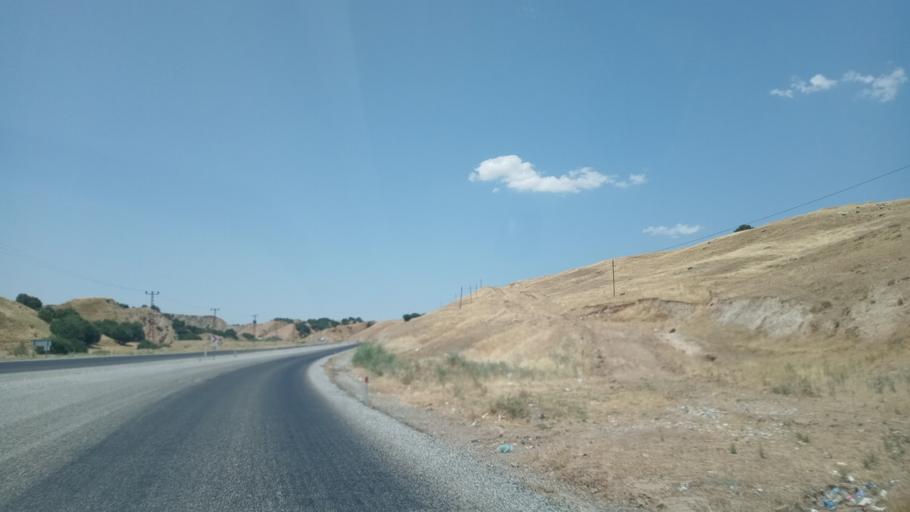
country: TR
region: Batman
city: Kozluk
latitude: 38.1679
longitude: 41.4696
